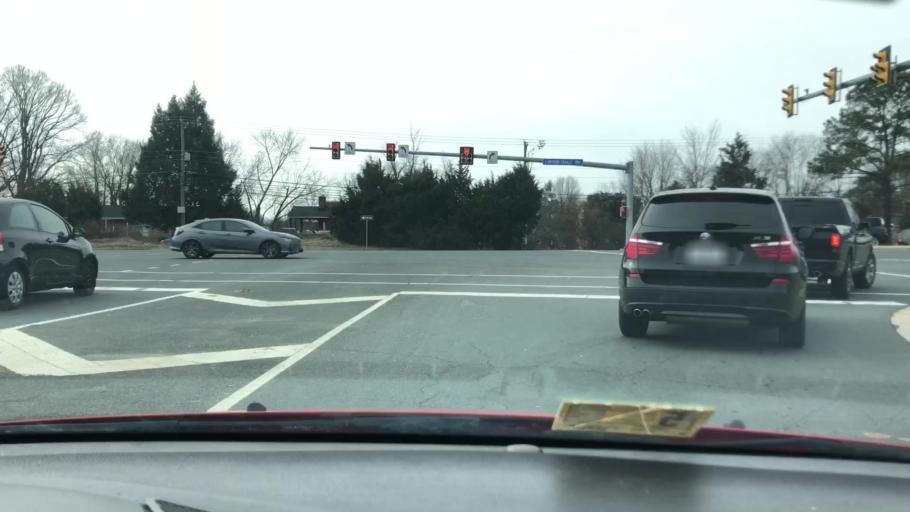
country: US
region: Virginia
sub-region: Prince William County
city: Gainesville
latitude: 38.7898
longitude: -77.6087
